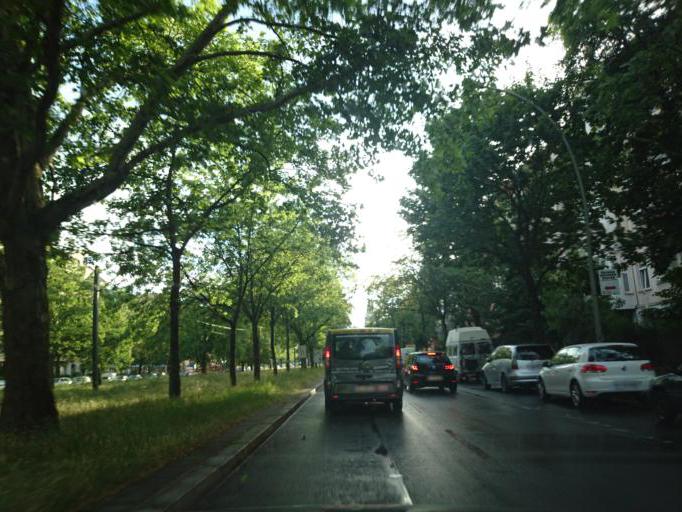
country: DE
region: Berlin
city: Gesundbrunnen
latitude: 52.5558
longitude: 13.3875
